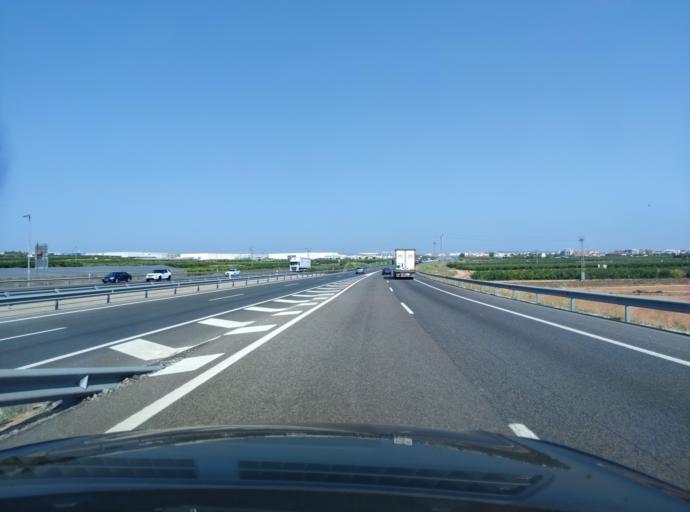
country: ES
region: Valencia
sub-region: Provincia de Valencia
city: Alcasser
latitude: 39.3517
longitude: -0.4324
